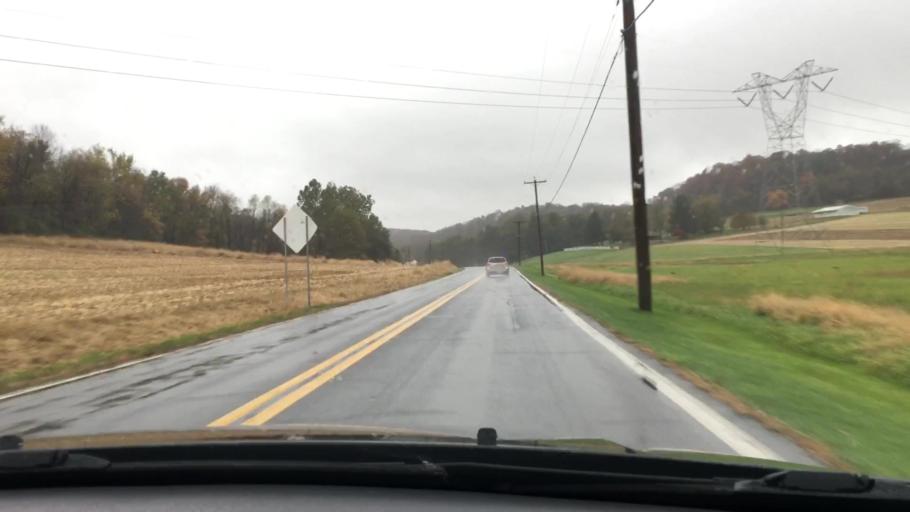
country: US
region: Maryland
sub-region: Carroll County
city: Manchester
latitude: 39.7079
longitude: -76.8561
